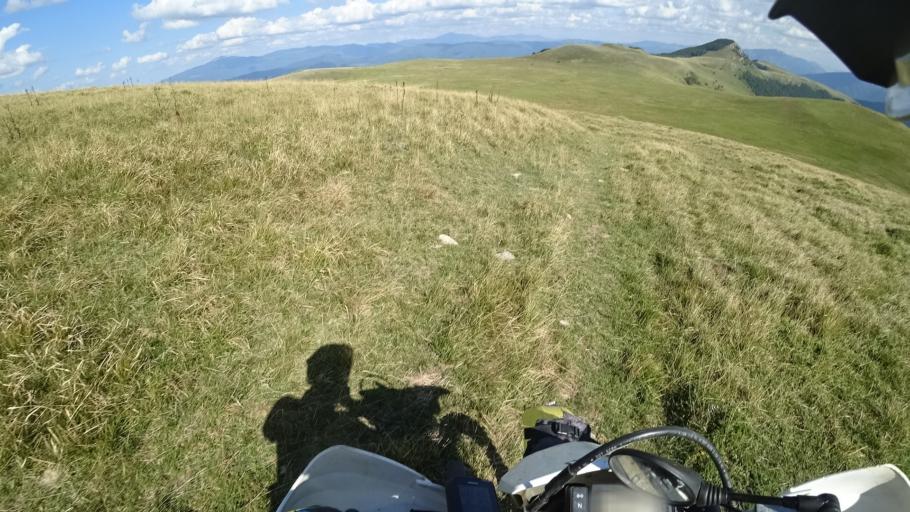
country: HR
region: Zadarska
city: Gracac
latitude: 44.3928
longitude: 16.0232
